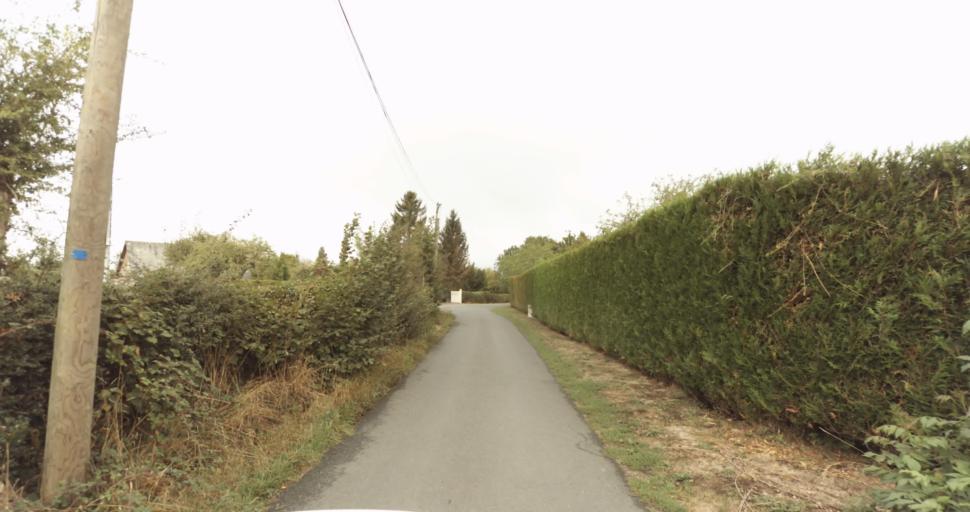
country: FR
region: Lower Normandy
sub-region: Departement de l'Orne
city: Vimoutiers
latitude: 48.9285
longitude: 0.1486
